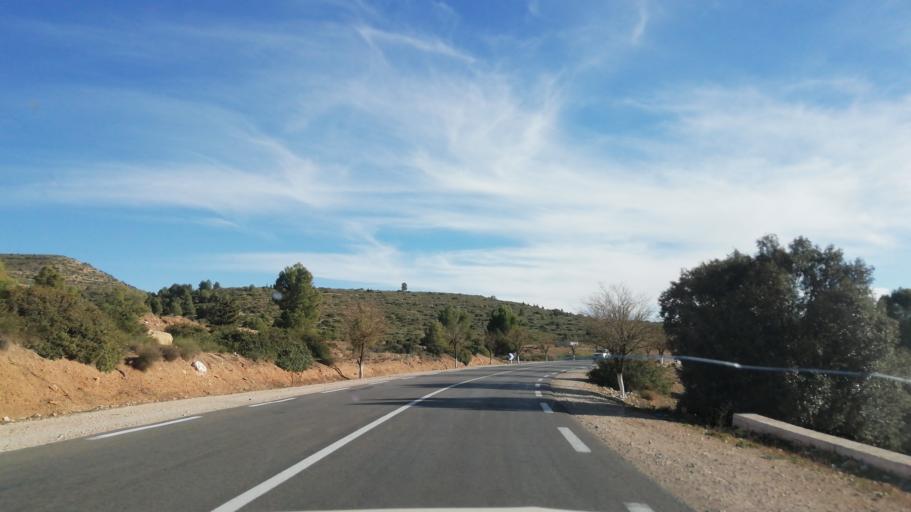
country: DZ
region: Tlemcen
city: Sebdou
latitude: 34.6022
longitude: -1.3247
